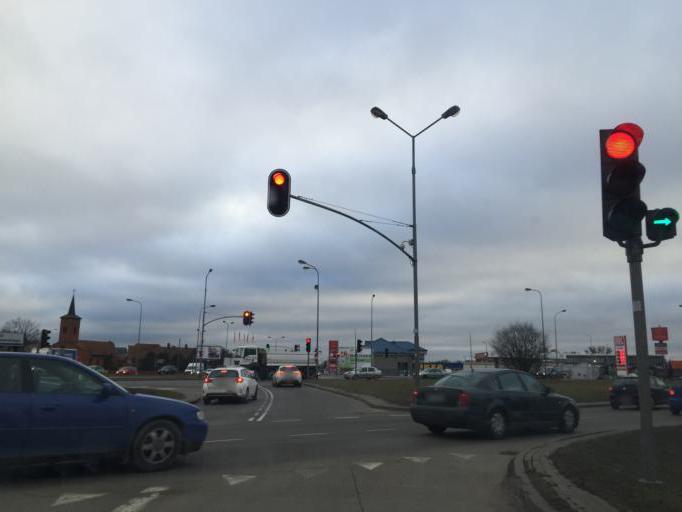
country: PL
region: Pomeranian Voivodeship
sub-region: Sopot
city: Sopot
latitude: 54.3767
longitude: 18.5224
